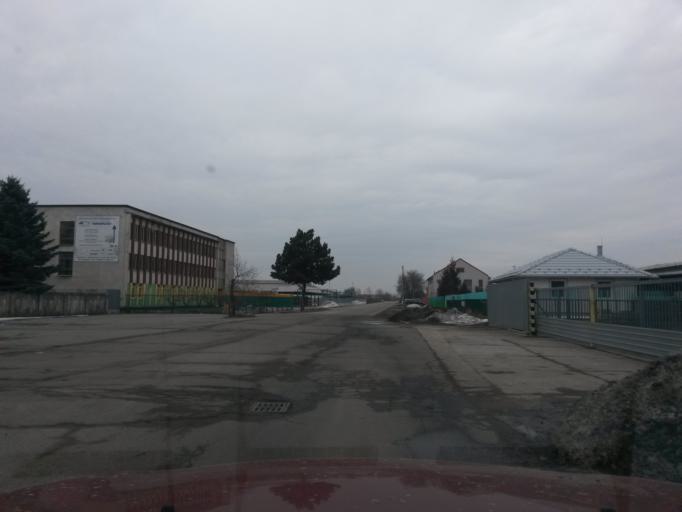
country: SK
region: Kosicky
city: Michalovce
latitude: 48.7466
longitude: 21.8898
